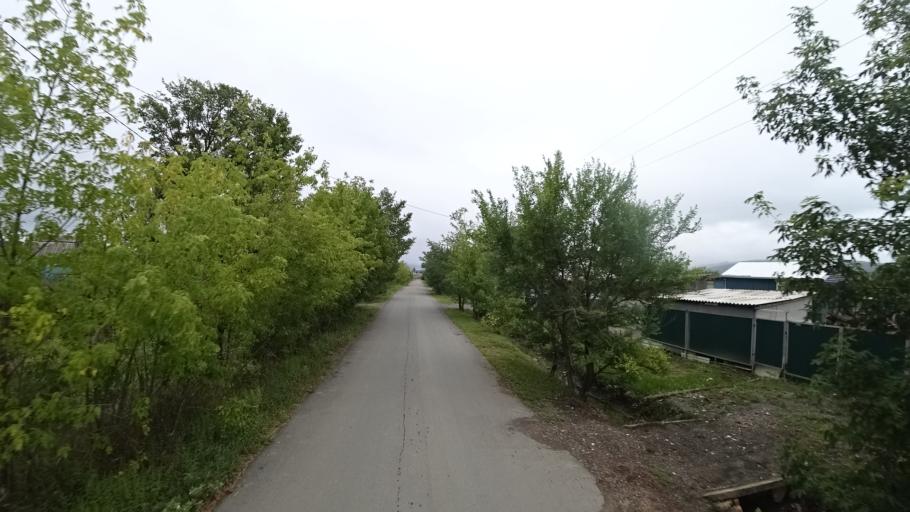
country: RU
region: Primorskiy
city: Chernigovka
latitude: 44.3280
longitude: 132.5979
